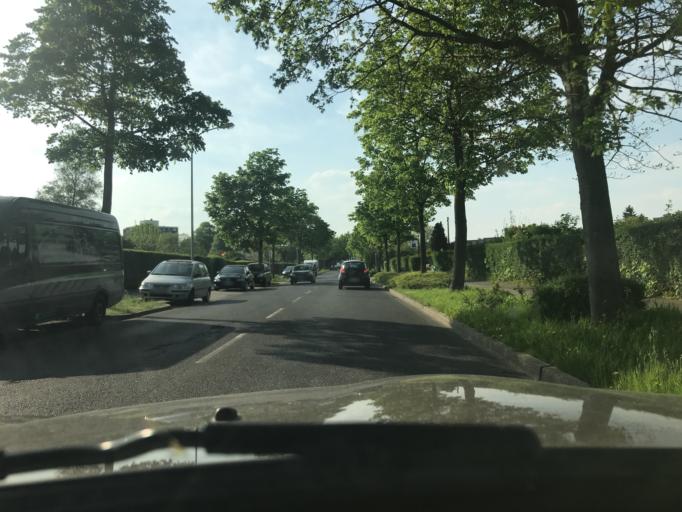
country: DE
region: North Rhine-Westphalia
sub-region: Regierungsbezirk Dusseldorf
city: Krefeld
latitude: 51.3090
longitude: 6.5738
